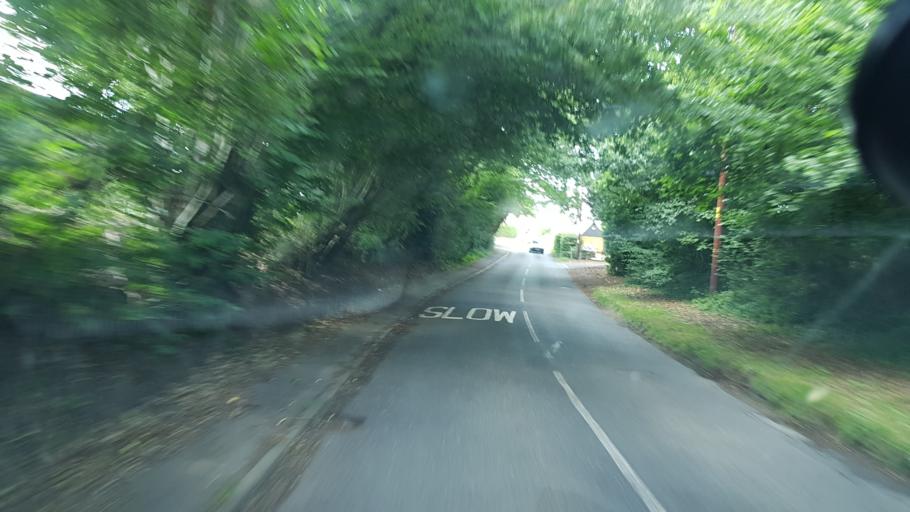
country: GB
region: England
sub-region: West Sussex
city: Rudgwick
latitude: 51.0843
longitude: -0.4561
